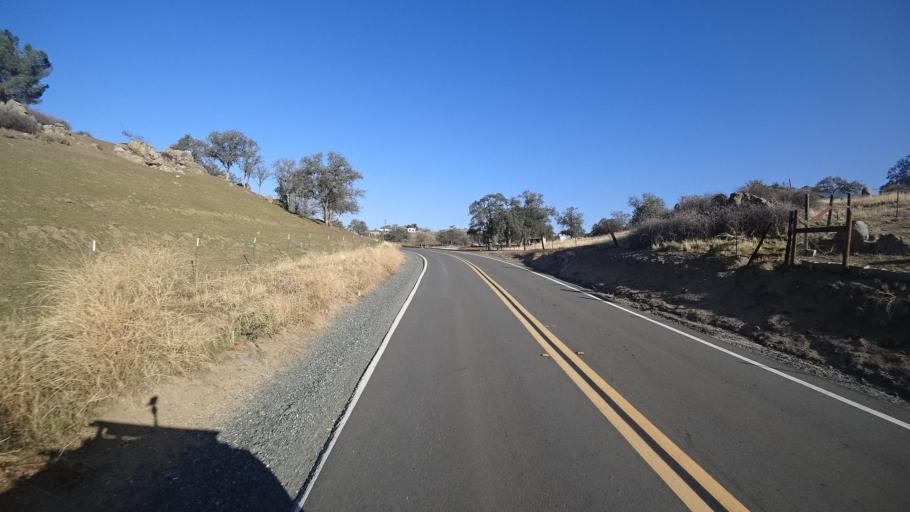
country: US
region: California
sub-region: Tulare County
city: Richgrove
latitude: 35.7067
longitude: -118.8364
